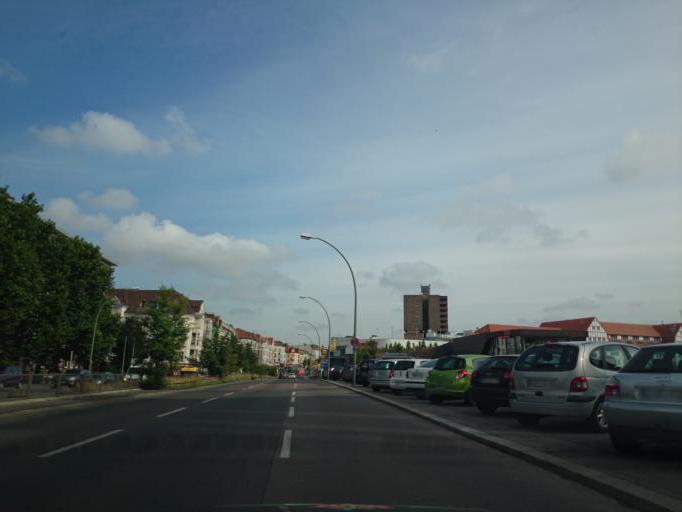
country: DE
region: Berlin
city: Mariendorf
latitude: 52.4537
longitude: 13.3844
